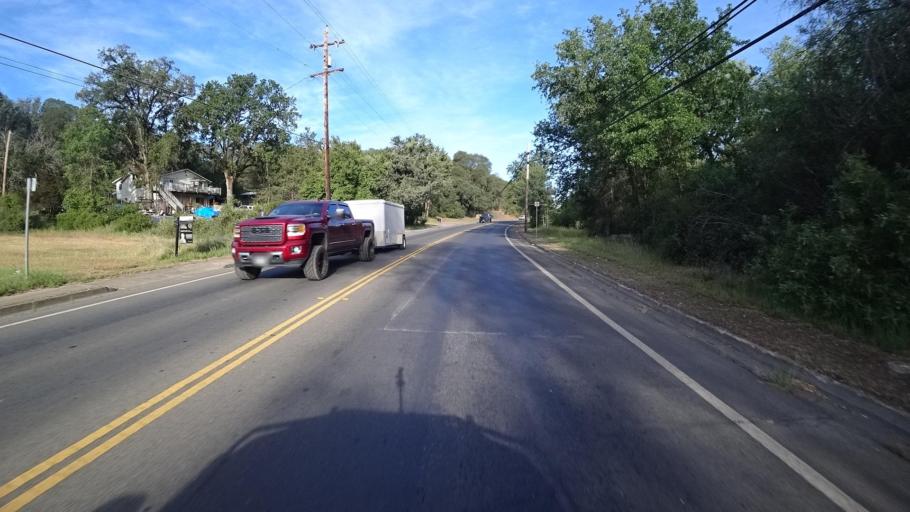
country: US
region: California
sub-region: Lake County
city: Lakeport
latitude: 39.0491
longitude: -122.9275
